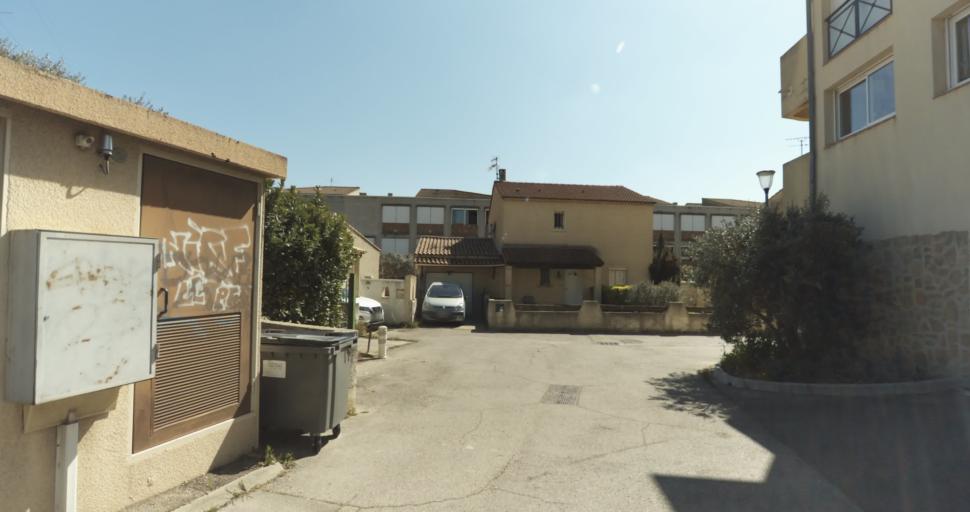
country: FR
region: Provence-Alpes-Cote d'Azur
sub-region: Departement des Bouches-du-Rhone
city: Pelissanne
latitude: 43.6332
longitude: 5.1557
